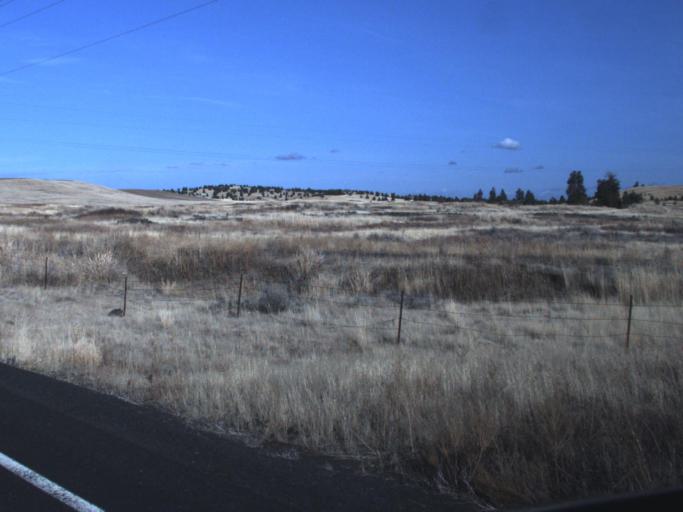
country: US
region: Washington
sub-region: Lincoln County
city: Davenport
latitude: 47.7589
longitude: -118.1735
